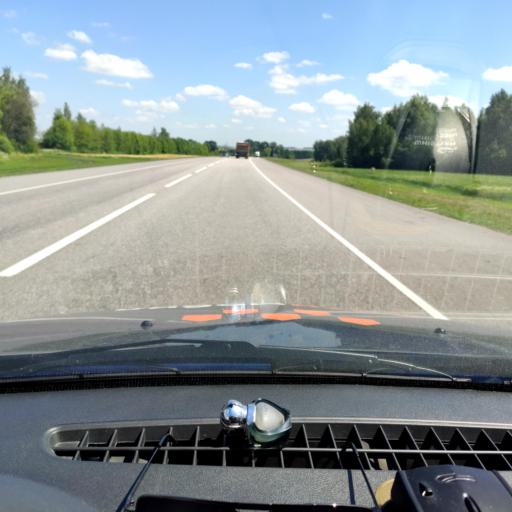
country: RU
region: Orjol
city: Orel
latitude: 52.8504
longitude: 36.2426
